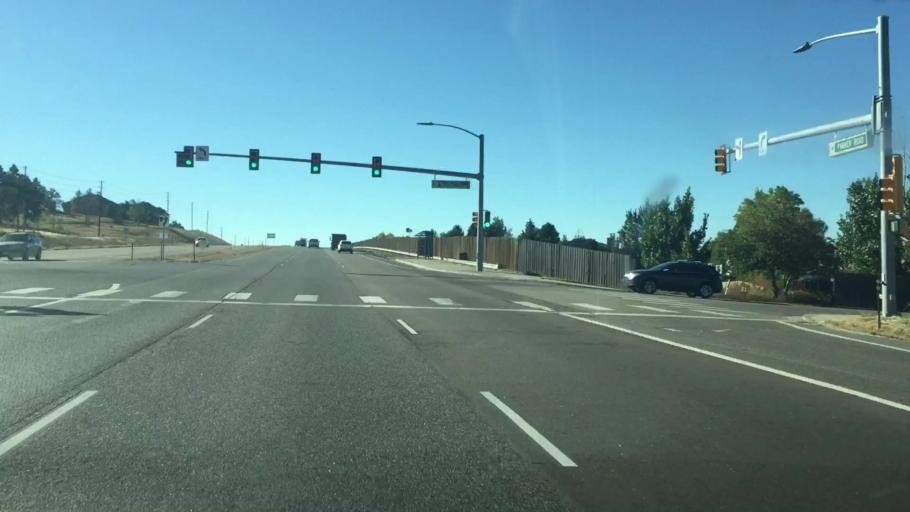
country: US
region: Colorado
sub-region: Douglas County
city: Parker
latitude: 39.5005
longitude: -104.7619
